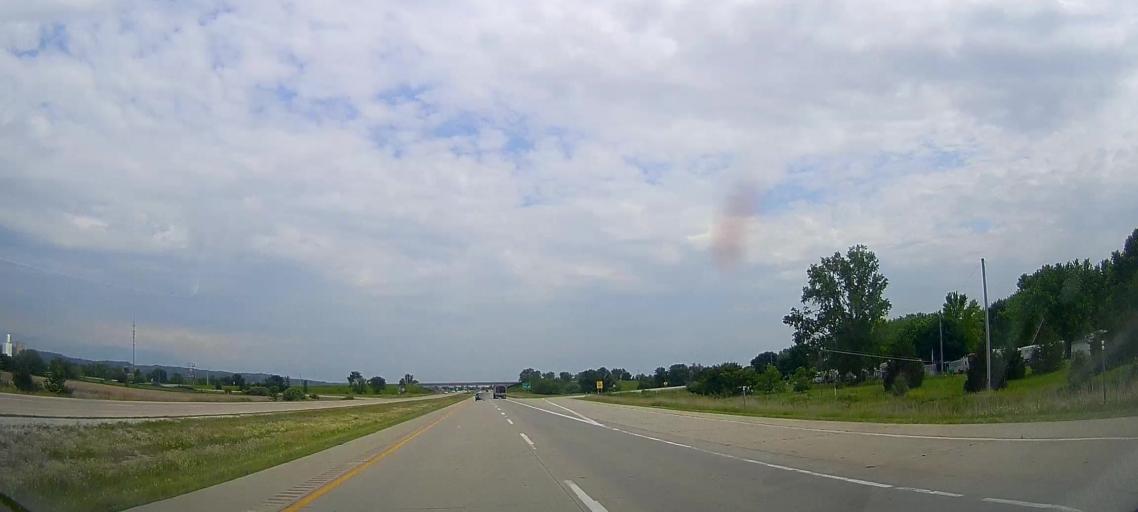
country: US
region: Nebraska
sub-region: Burt County
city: Tekamah
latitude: 41.8049
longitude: -96.0585
